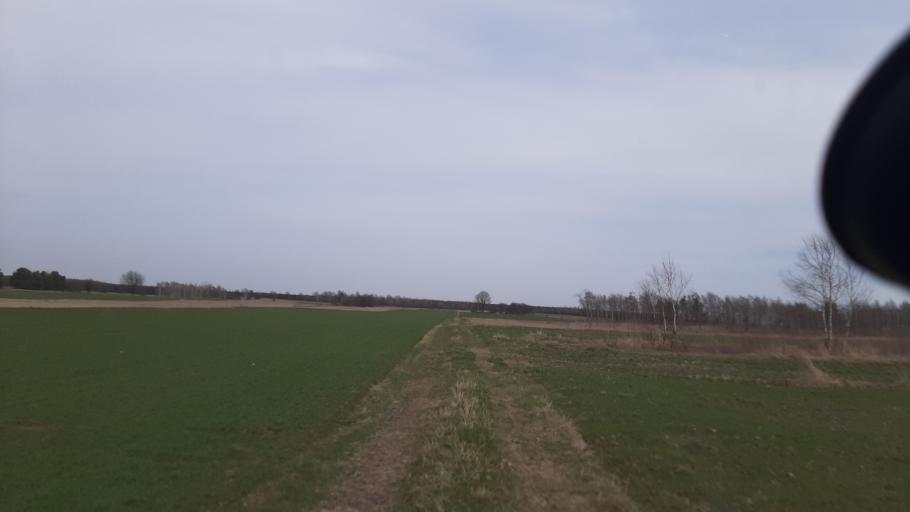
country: PL
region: Lublin Voivodeship
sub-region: Powiat lubelski
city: Jastkow
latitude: 51.3758
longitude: 22.4228
